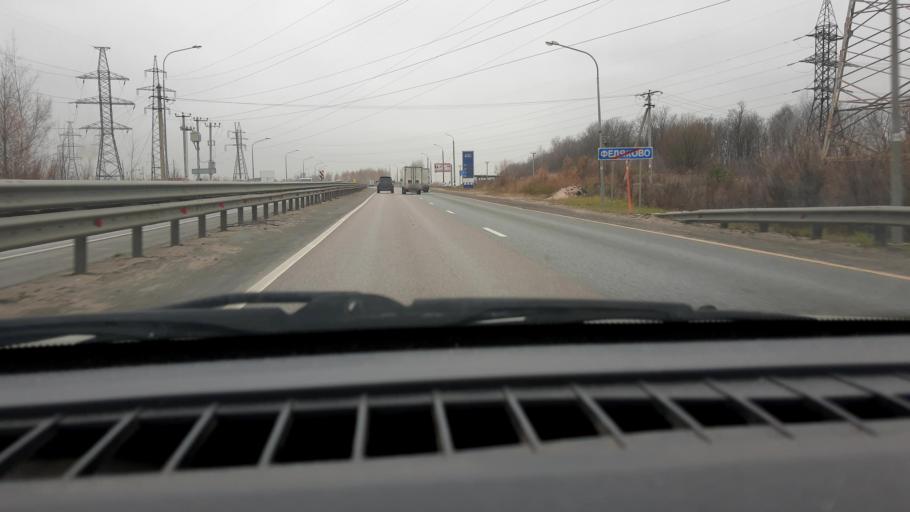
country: RU
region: Nizjnij Novgorod
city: Afonino
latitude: 56.2336
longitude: 44.0522
